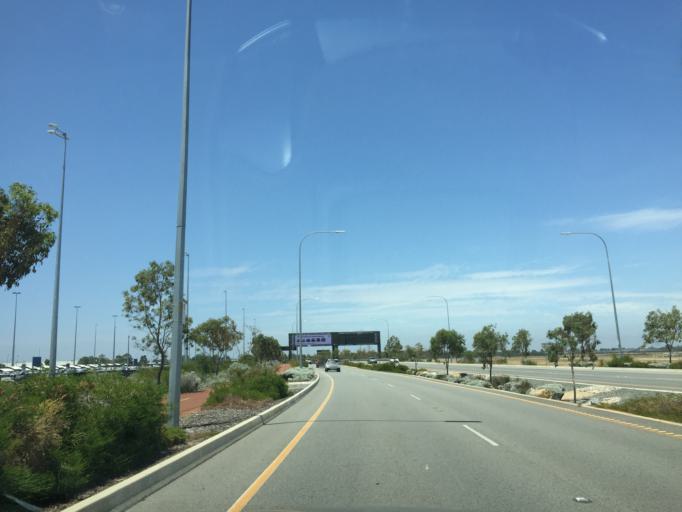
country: AU
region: Western Australia
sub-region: Belmont
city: Redcliffe
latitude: -31.9505
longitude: 115.9705
